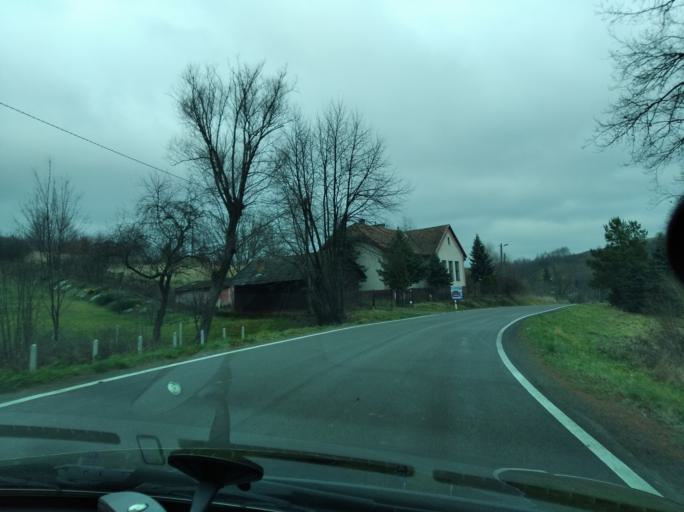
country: PL
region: Subcarpathian Voivodeship
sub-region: Powiat przeworski
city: Jawornik Polski
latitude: 49.9158
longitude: 22.3008
